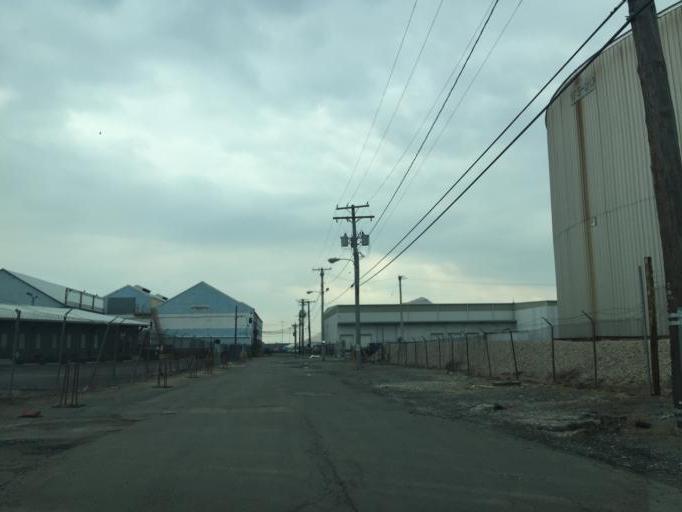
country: US
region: Maryland
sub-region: Baltimore County
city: Dundalk
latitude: 39.2743
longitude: -76.5616
